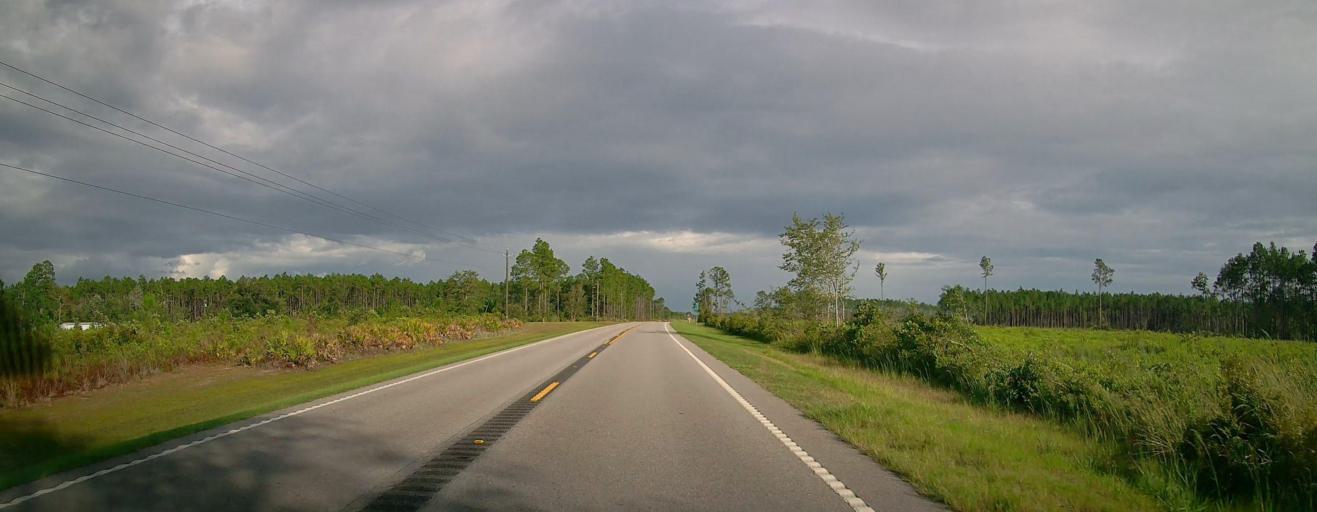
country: US
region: Georgia
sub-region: Coffee County
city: Nicholls
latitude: 31.3810
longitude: -82.6438
